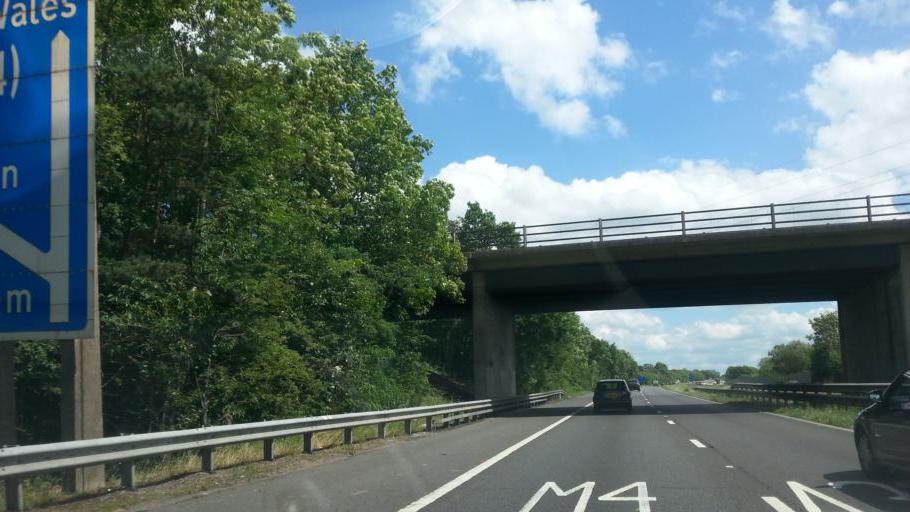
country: GB
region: England
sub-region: Wokingham
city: Winnersh
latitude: 51.4381
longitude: -0.8728
